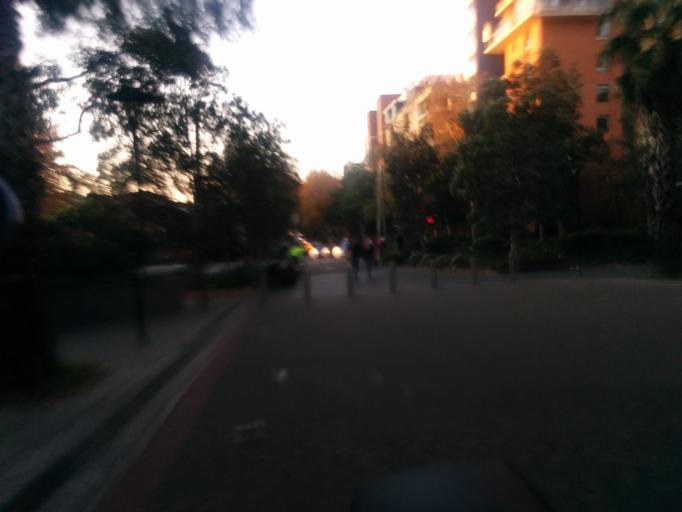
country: AU
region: New South Wales
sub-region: City of Sydney
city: Redfern
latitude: -33.8976
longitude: 151.2132
